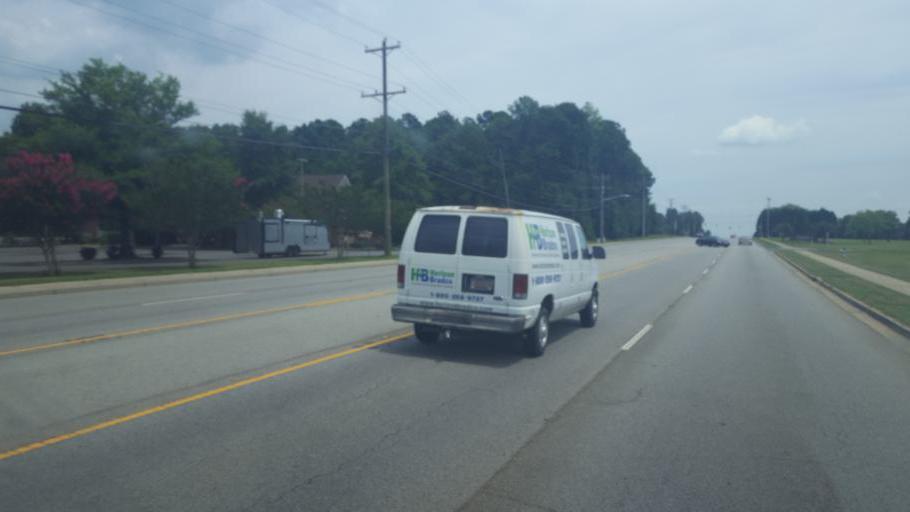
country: US
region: South Carolina
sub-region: York County
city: Newport
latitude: 34.9485
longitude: -81.0782
